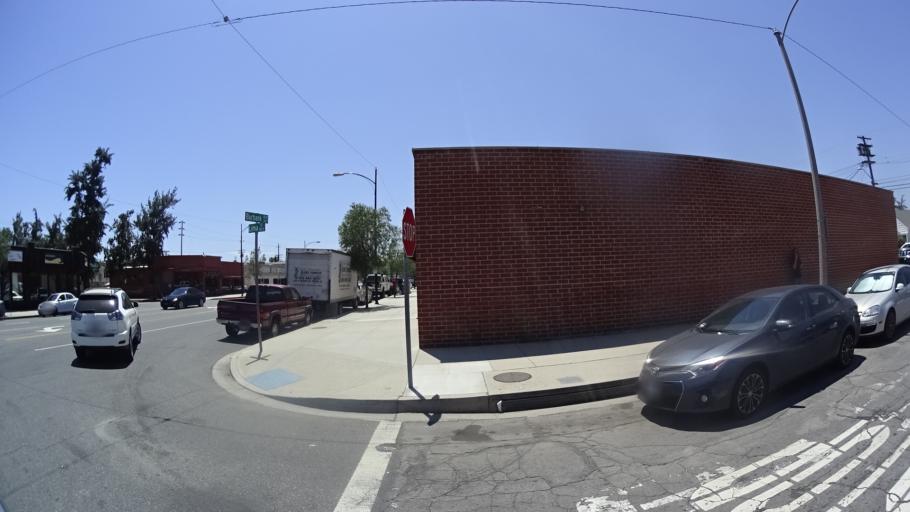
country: US
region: California
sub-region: Los Angeles County
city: North Hollywood
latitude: 34.1759
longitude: -118.3470
